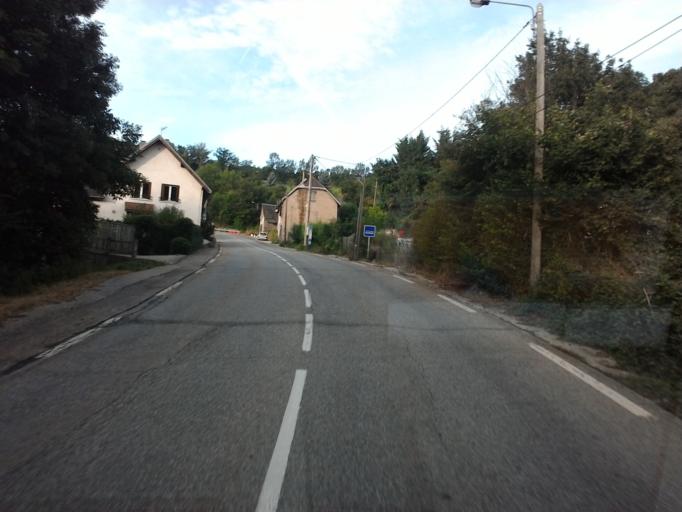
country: FR
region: Rhone-Alpes
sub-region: Departement de l'Isere
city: La Mure
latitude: 44.9004
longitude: 5.8083
